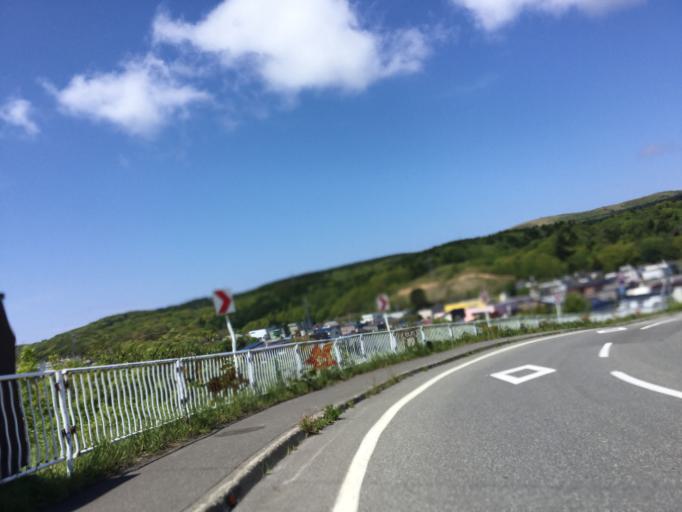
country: JP
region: Hokkaido
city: Wakkanai
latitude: 45.3888
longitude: 141.6823
